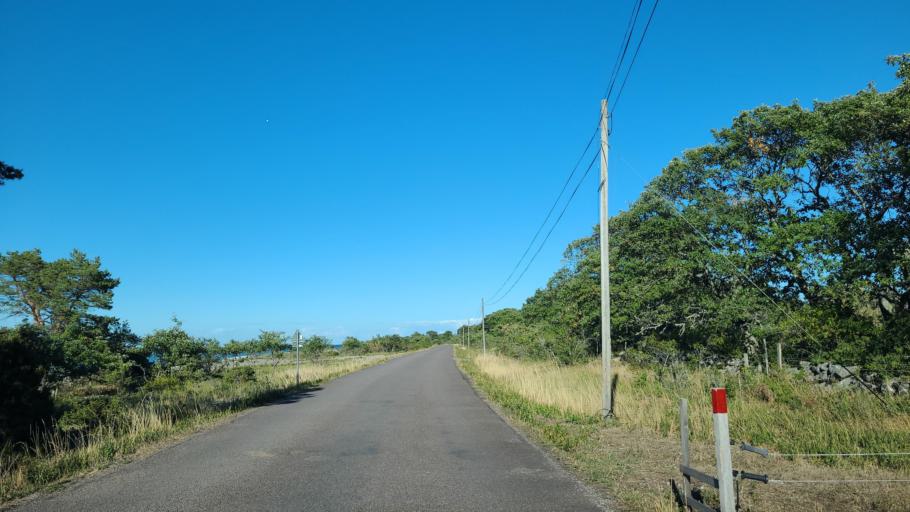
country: SE
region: Kalmar
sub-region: Vasterviks Kommun
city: Vaestervik
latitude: 57.3658
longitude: 17.0712
